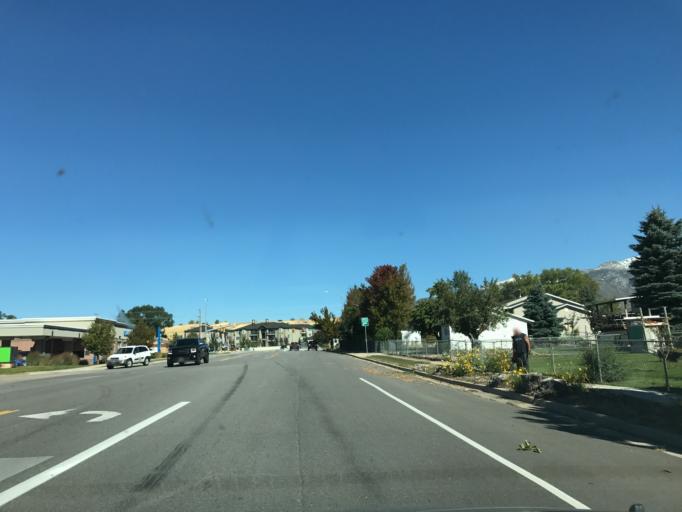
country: US
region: Utah
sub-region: Davis County
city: South Weber
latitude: 41.0999
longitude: -111.9391
